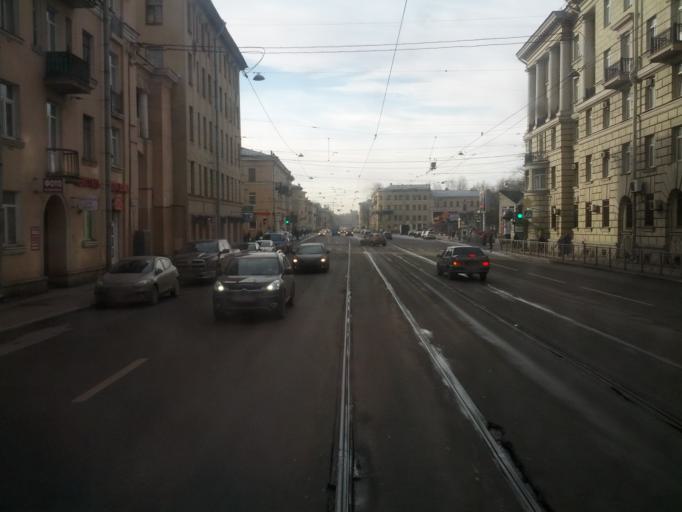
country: RU
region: Leningrad
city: Kalininskiy
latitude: 59.9541
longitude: 30.4151
